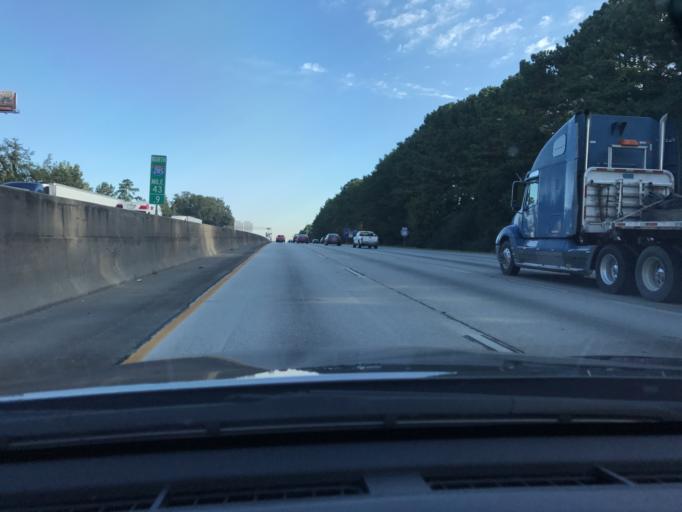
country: US
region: Georgia
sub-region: DeKalb County
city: Belvedere Park
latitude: 33.7437
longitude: -84.2305
